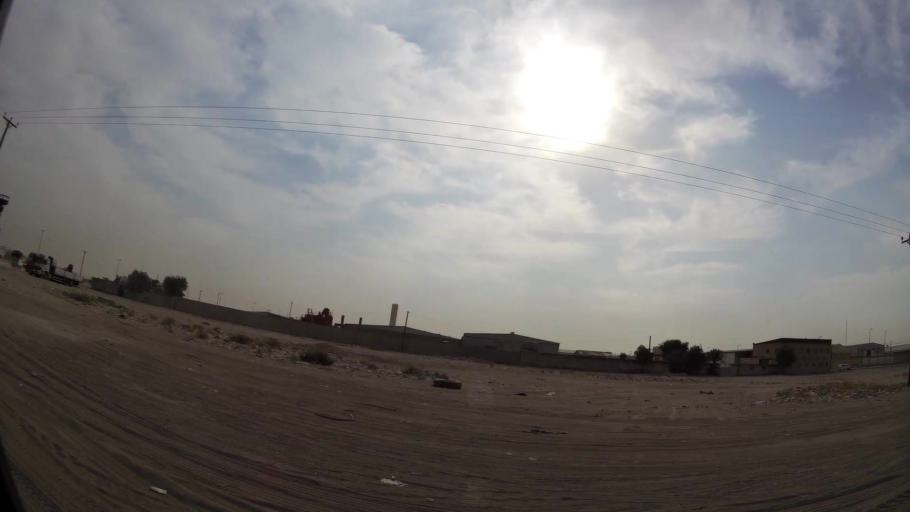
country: KW
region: Muhafazat al Jahra'
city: Al Jahra'
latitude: 29.3148
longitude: 47.7459
